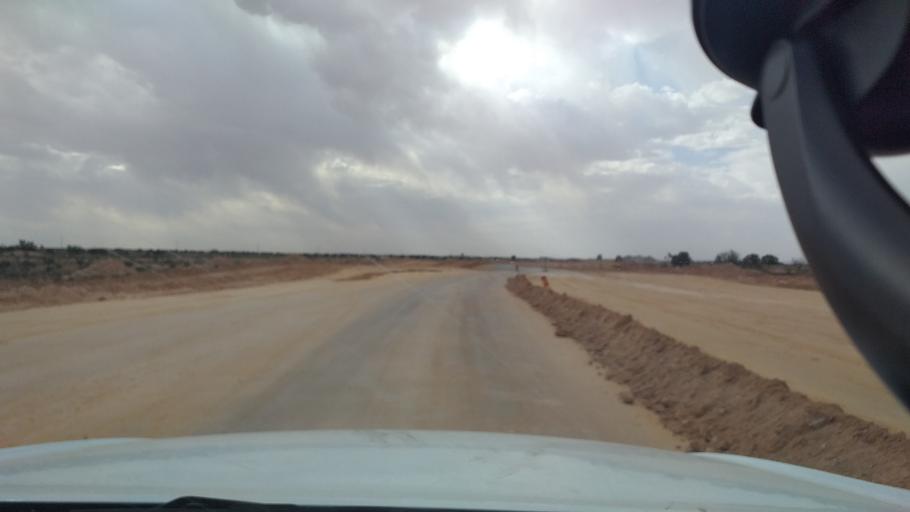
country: TN
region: Madanin
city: Medenine
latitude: 33.3072
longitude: 10.6134
